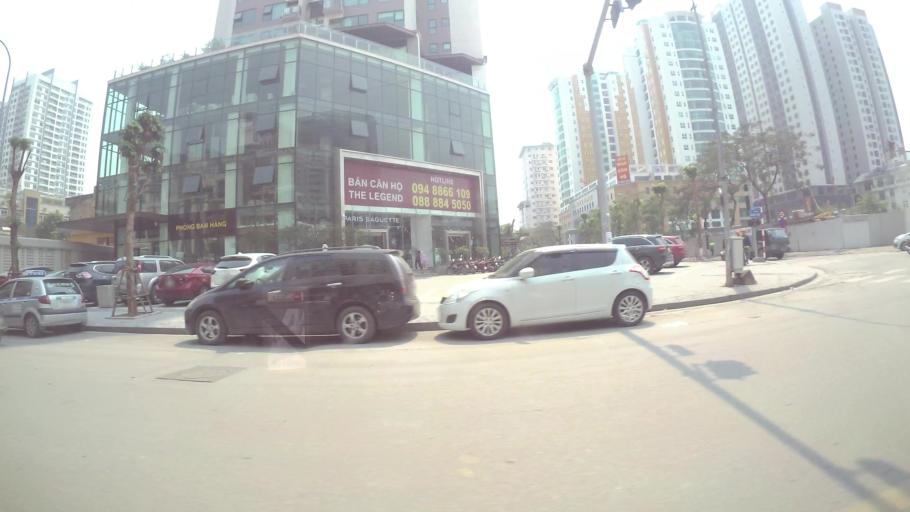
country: VN
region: Ha Noi
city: Thanh Xuan
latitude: 20.9999
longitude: 105.8021
